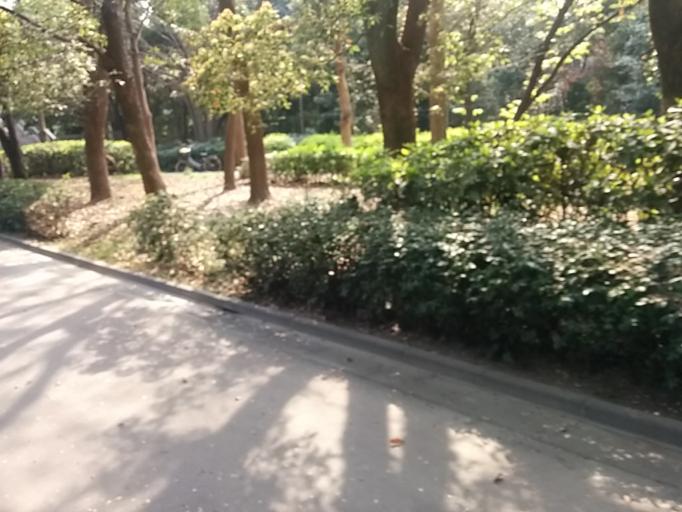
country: JP
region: Tokyo
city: Urayasu
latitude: 35.6498
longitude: 139.8564
